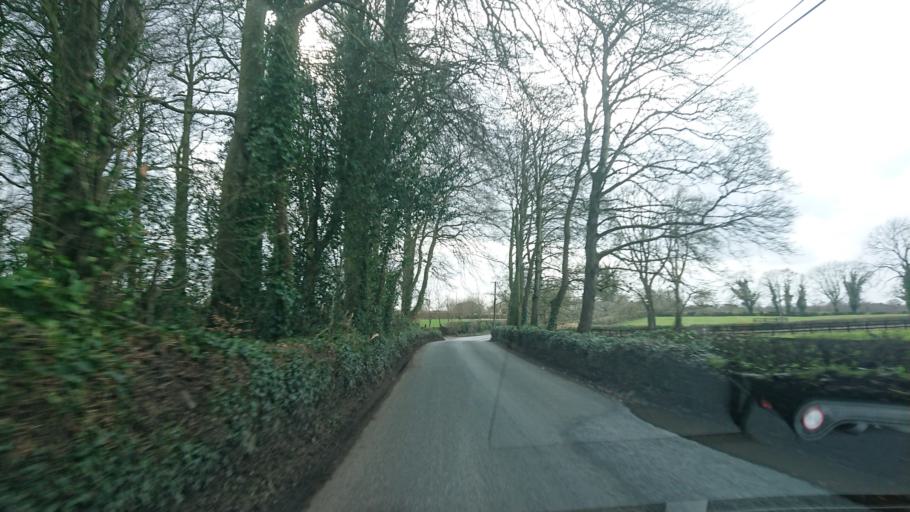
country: IE
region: Leinster
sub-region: Kildare
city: Naas
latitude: 53.1834
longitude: -6.6518
